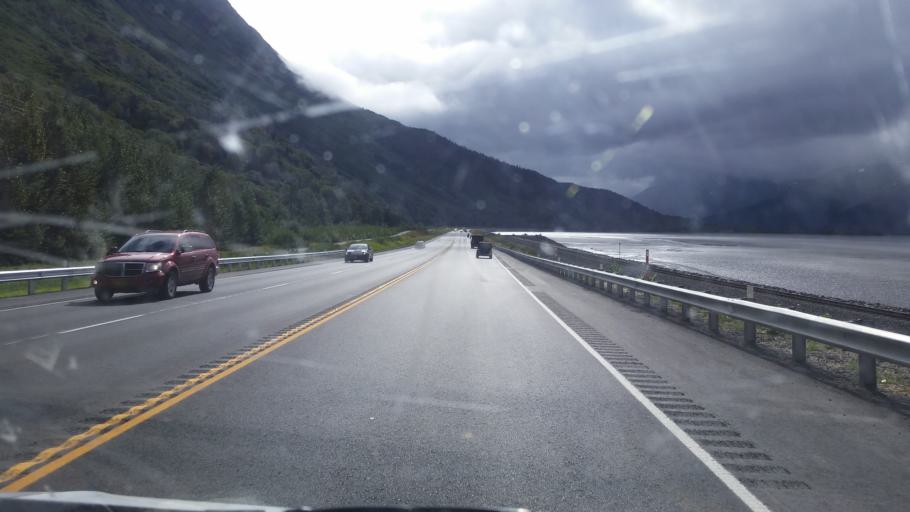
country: US
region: Alaska
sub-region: Anchorage Municipality
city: Girdwood
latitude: 60.9515
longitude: -149.4051
